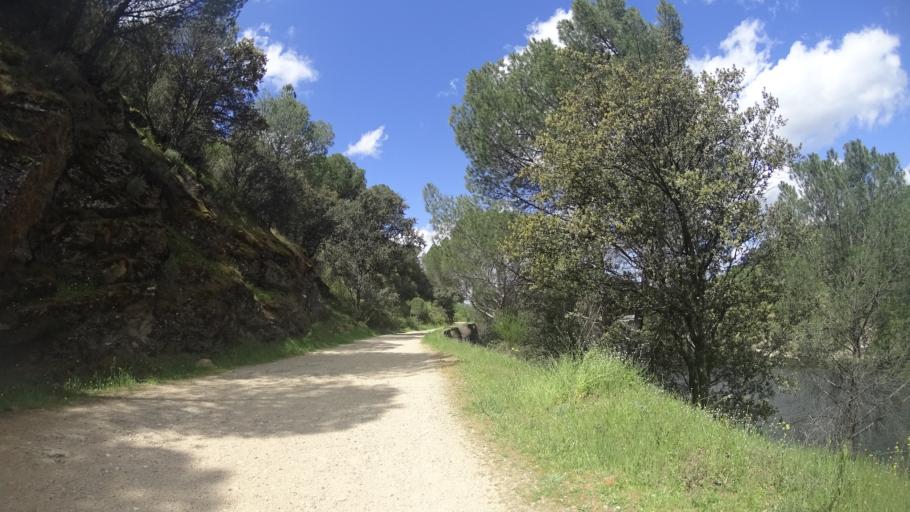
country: ES
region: Madrid
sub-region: Provincia de Madrid
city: Pelayos de la Presa
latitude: 40.3660
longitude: -4.3005
